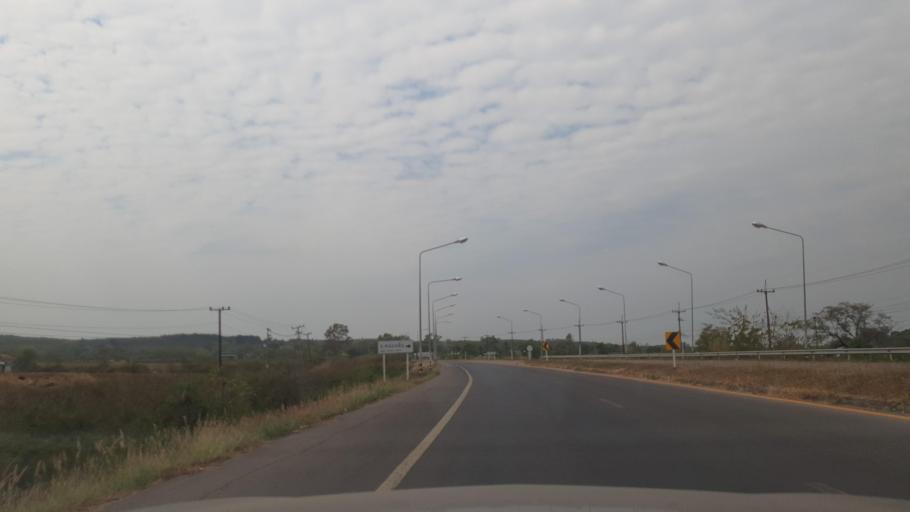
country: TH
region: Changwat Bueng Kan
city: Bung Khla
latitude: 18.3058
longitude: 103.9707
